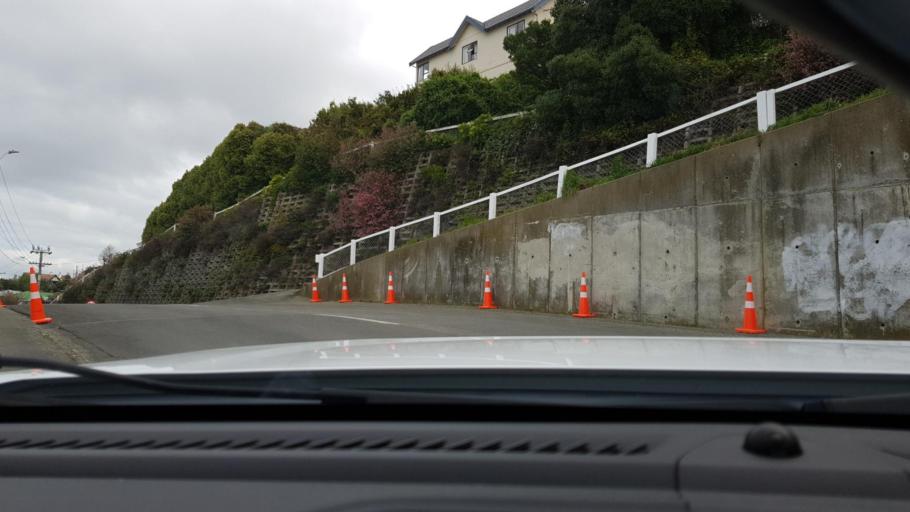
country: NZ
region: Otago
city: Oamaru
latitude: -45.0868
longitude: 170.9734
